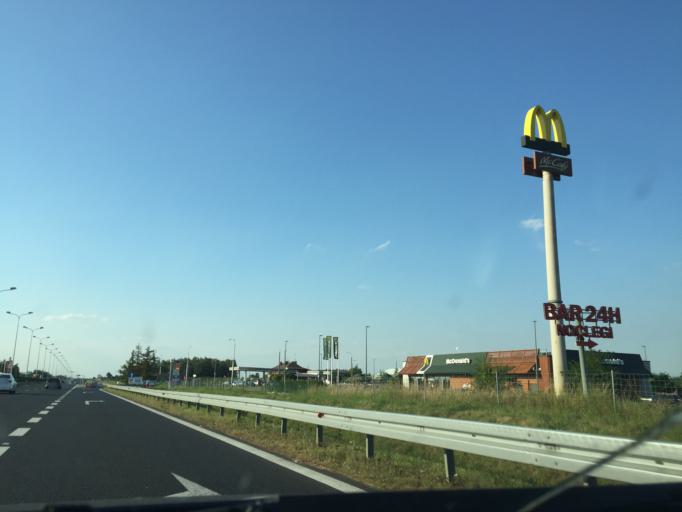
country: PL
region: Masovian Voivodeship
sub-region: Powiat grojecki
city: Goszczyn
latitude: 51.7438
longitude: 20.9114
